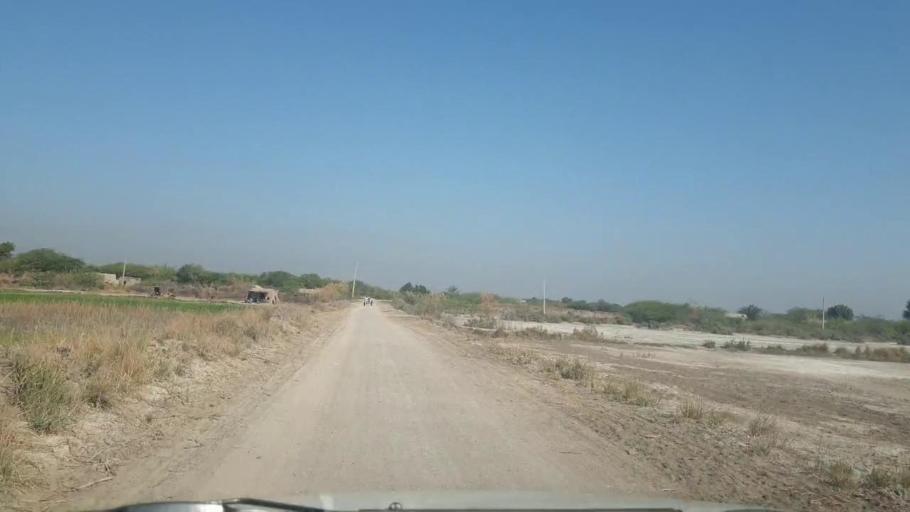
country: PK
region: Sindh
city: Mirpur Khas
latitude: 25.5143
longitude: 69.1493
